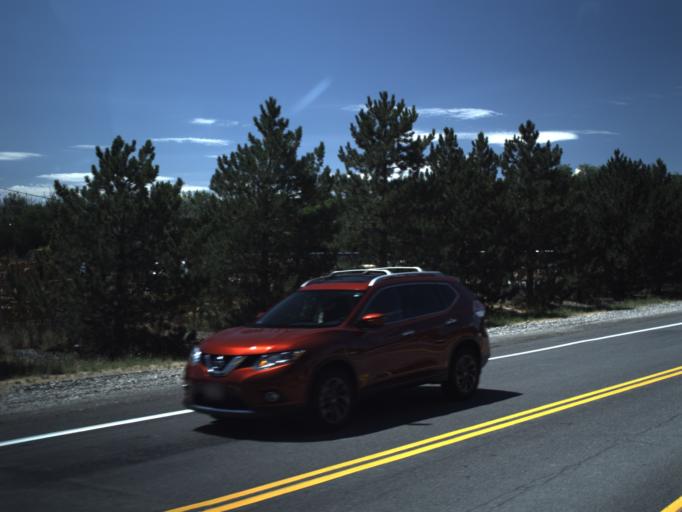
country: US
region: Utah
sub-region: Utah County
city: Springville
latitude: 40.1857
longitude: -111.6122
